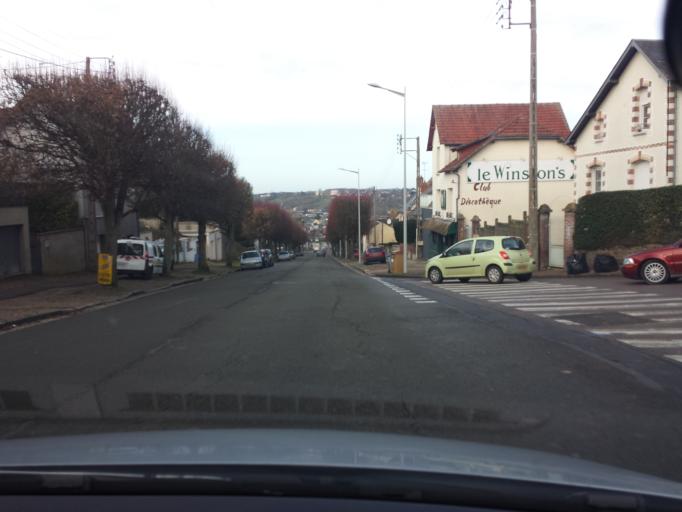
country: FR
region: Haute-Normandie
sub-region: Departement de l'Eure
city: Evreux
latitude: 49.0193
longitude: 1.1623
